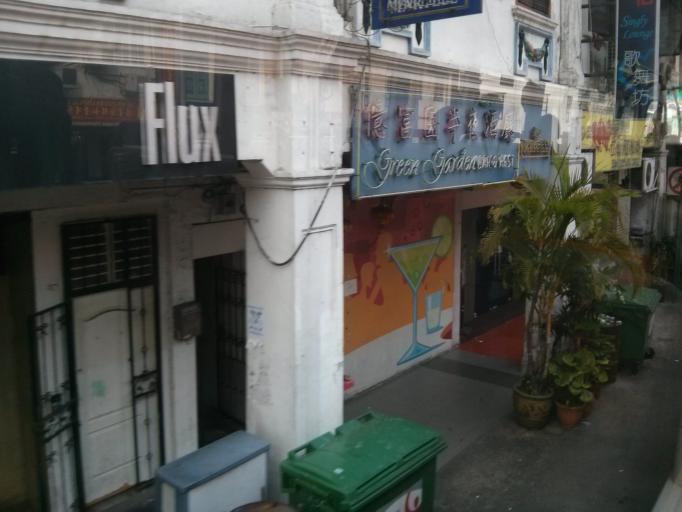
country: SG
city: Singapore
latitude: 1.3149
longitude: 103.8577
